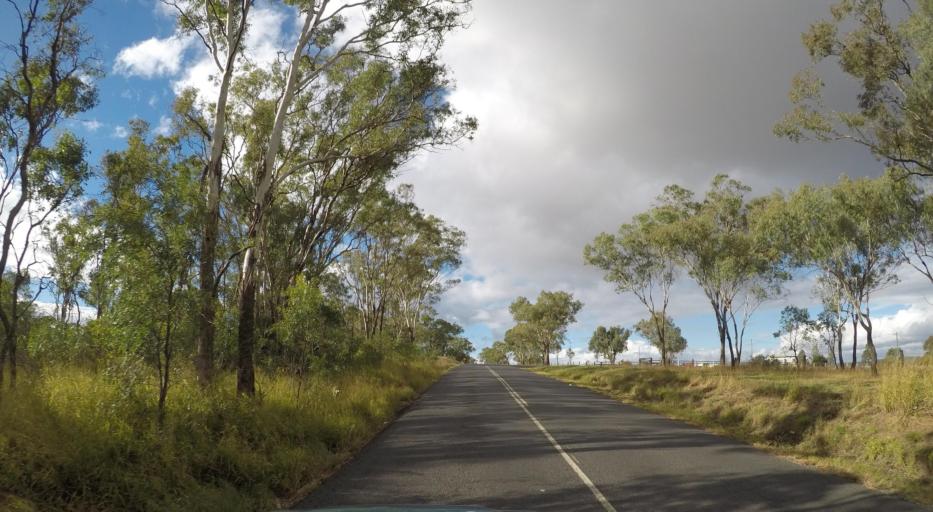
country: AU
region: Queensland
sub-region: Toowoomba
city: Westbrook
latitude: -27.6995
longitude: 151.6634
